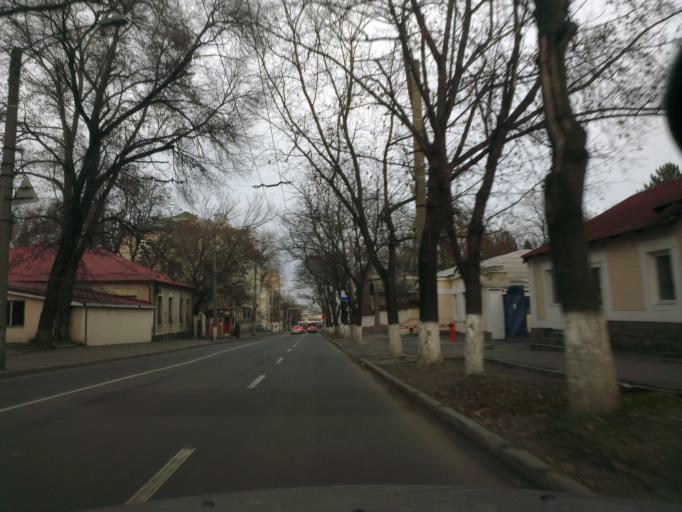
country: MD
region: Chisinau
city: Chisinau
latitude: 47.0328
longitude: 28.8170
